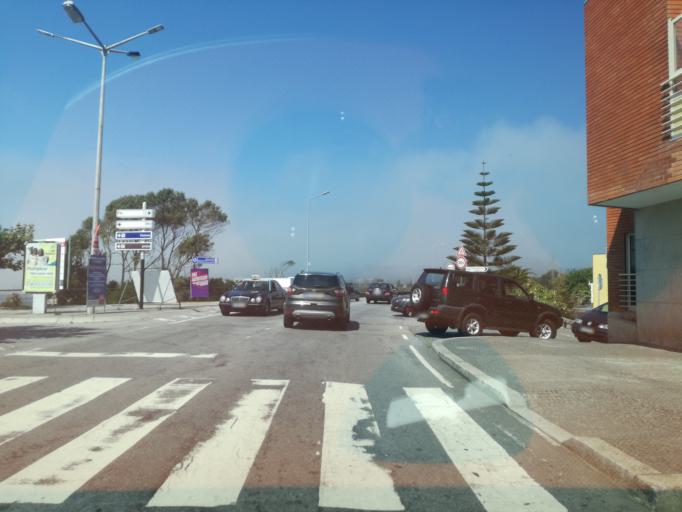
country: PT
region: Braga
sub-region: Esposende
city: Esposende
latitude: 41.5136
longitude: -8.7735
